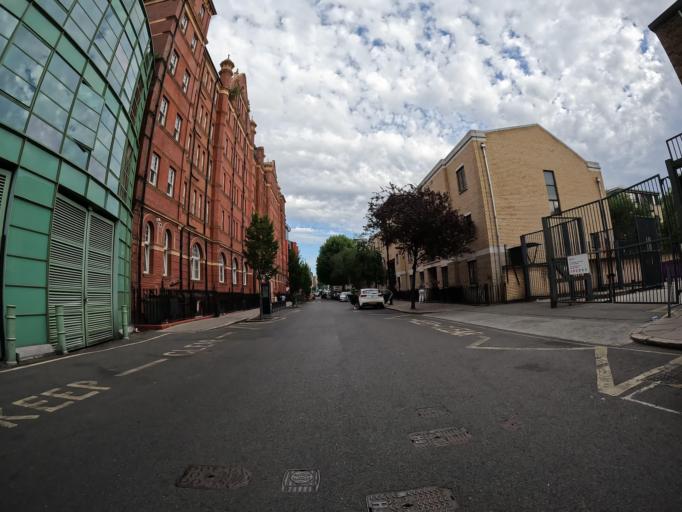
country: GB
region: England
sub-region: Greater London
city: Camden Town
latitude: 51.5401
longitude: -0.1453
